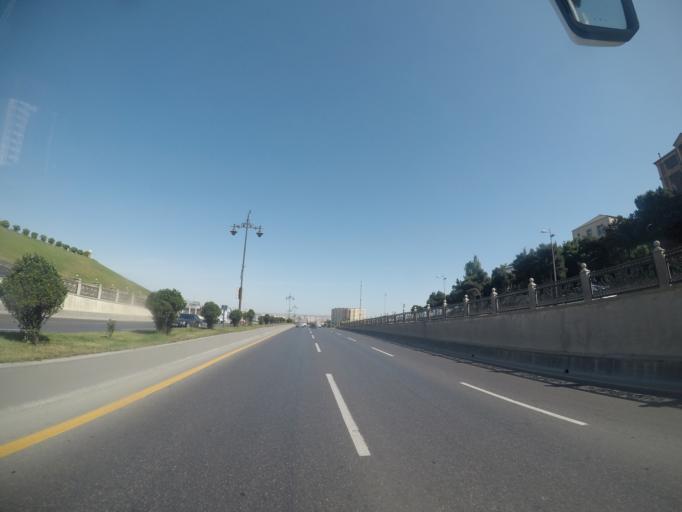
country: AZ
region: Baki
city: Bilajari
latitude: 40.4145
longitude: 49.8015
